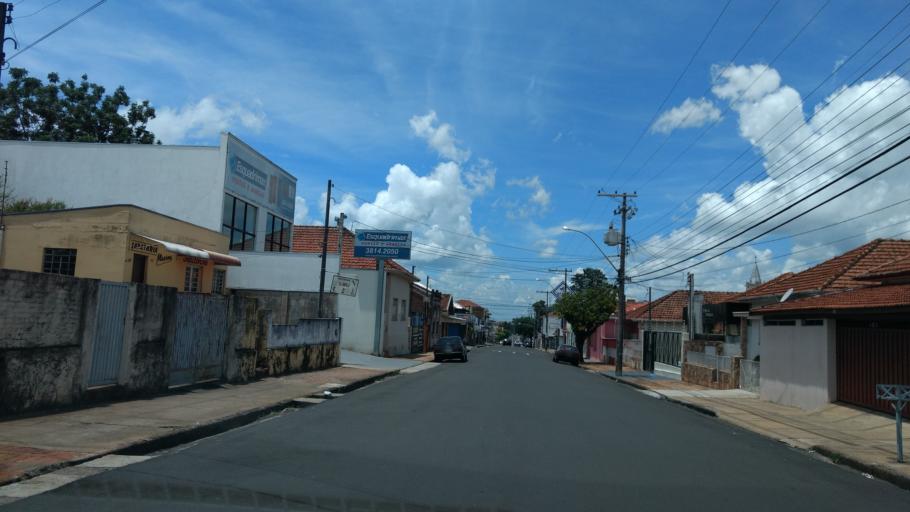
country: BR
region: Sao Paulo
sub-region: Botucatu
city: Botucatu
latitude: -22.8722
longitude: -48.4498
